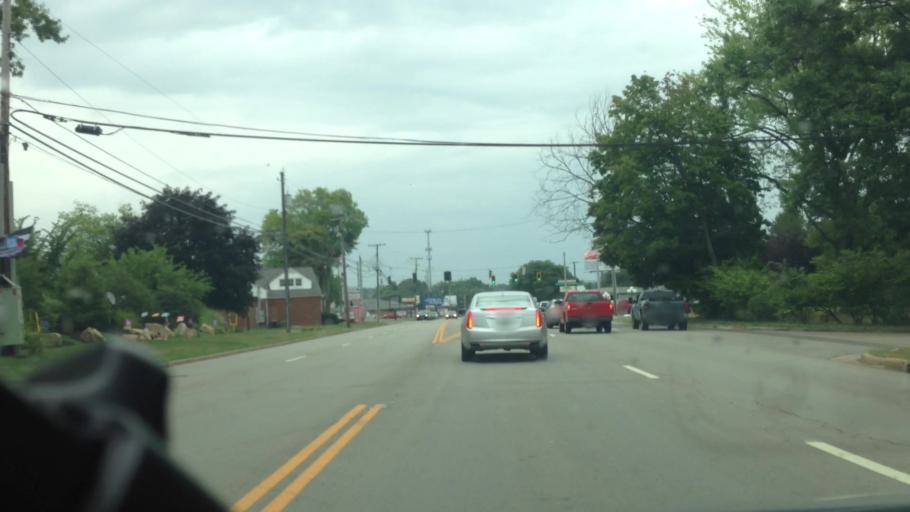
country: US
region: Ohio
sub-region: Stark County
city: Canton
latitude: 40.8277
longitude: -81.4051
